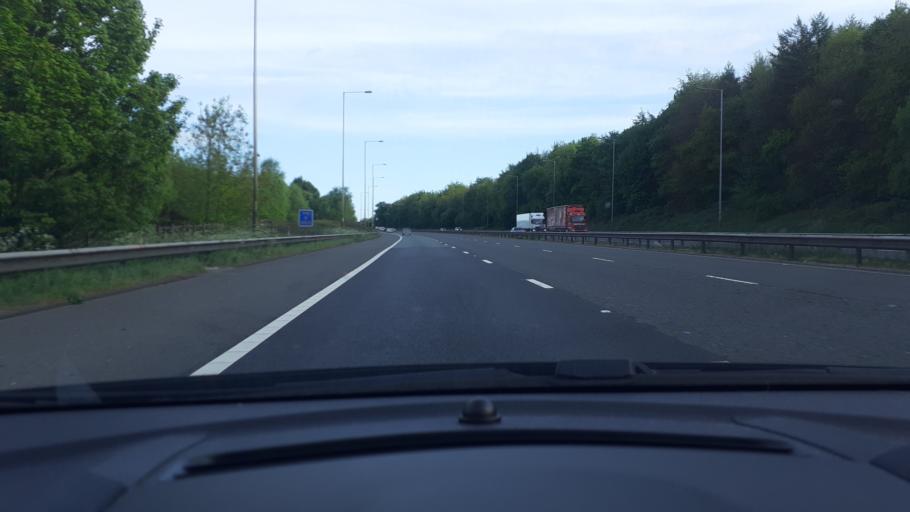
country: GB
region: England
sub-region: St. Helens
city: Billinge
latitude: 53.5212
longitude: -2.6963
